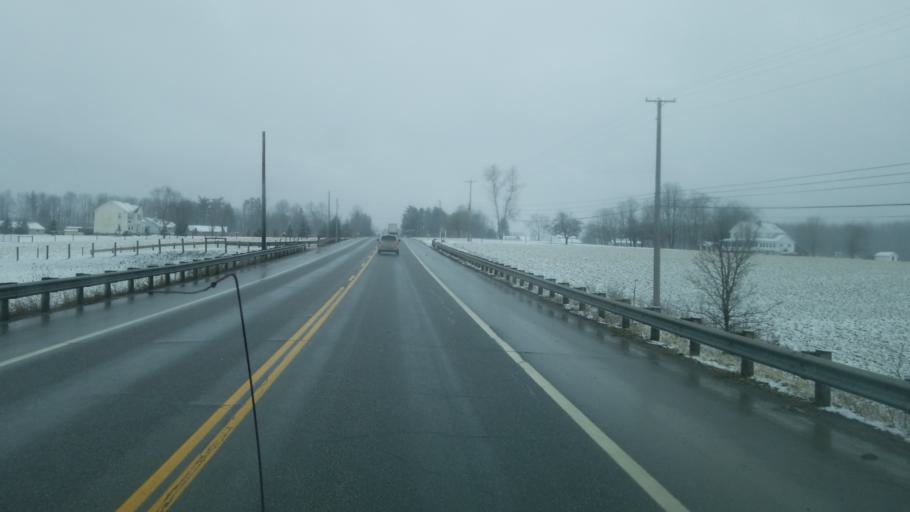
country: US
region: Ohio
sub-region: Geauga County
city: Middlefield
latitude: 41.3856
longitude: -81.0617
